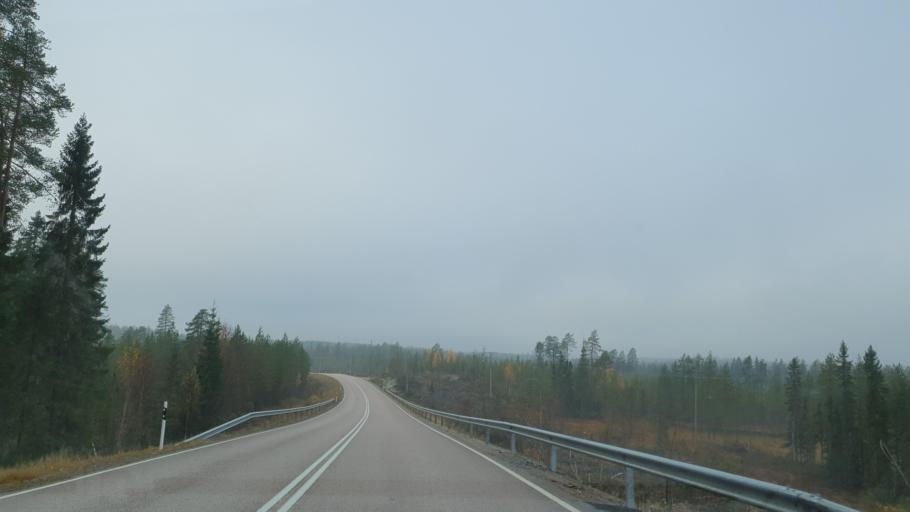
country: FI
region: Kainuu
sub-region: Kehys-Kainuu
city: Kuhmo
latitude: 64.4616
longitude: 29.5708
